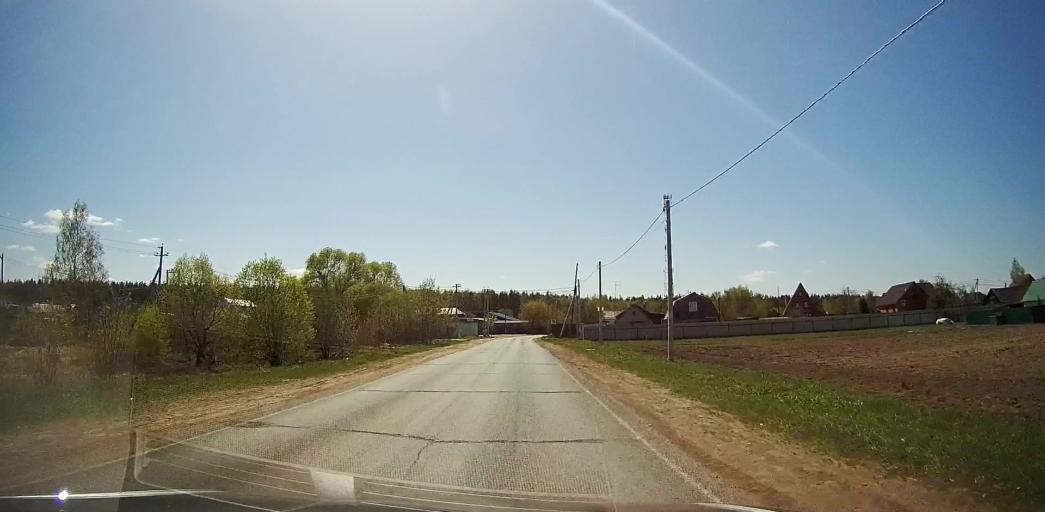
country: RU
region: Moskovskaya
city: Bronnitsy
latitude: 55.4557
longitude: 38.3019
